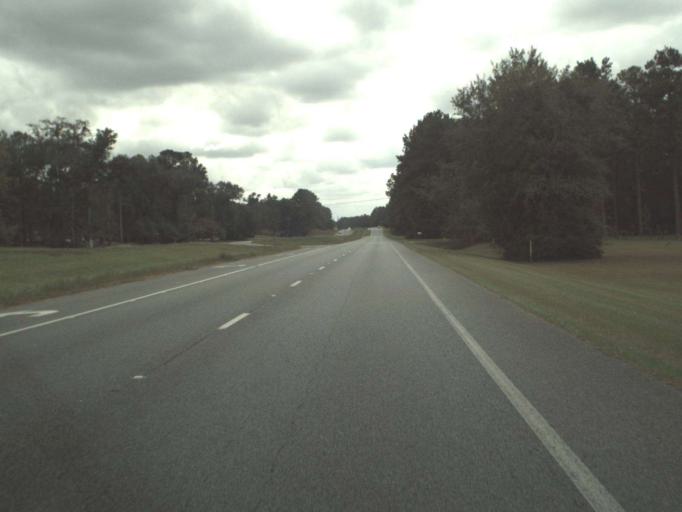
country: US
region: Florida
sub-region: Jefferson County
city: Monticello
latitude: 30.6153
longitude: -83.8724
